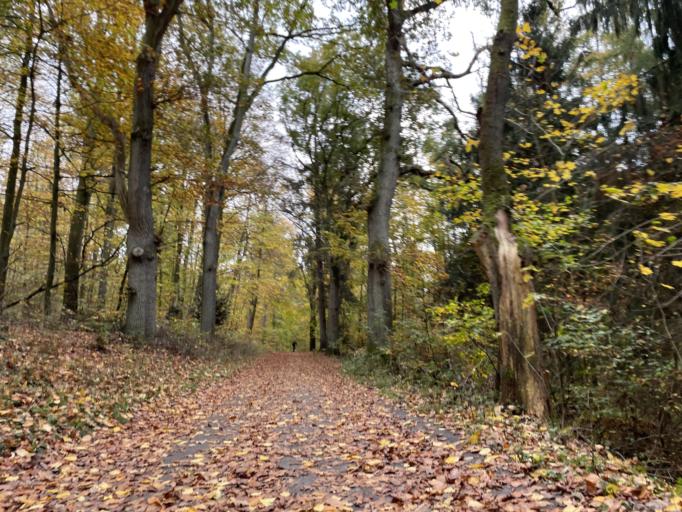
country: DE
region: Lower Saxony
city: Lueneburg
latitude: 53.2192
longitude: 10.3979
